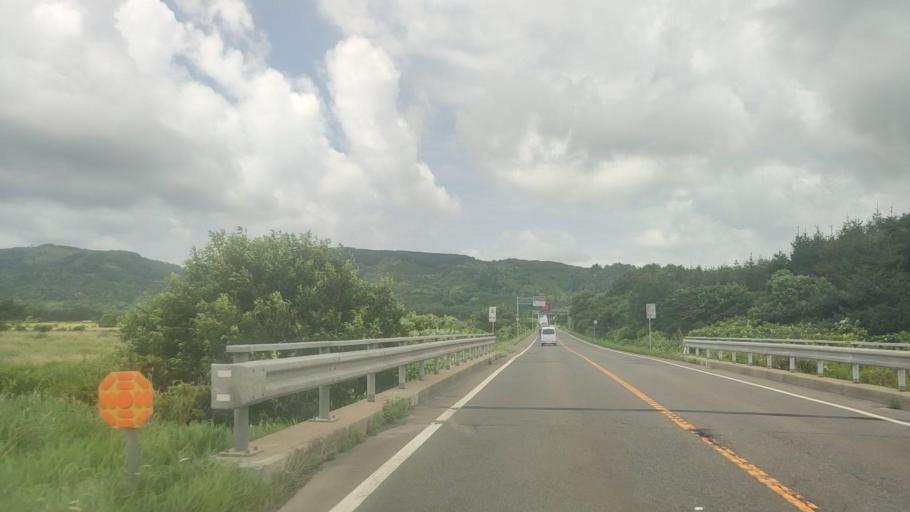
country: JP
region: Hokkaido
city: Niseko Town
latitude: 42.5822
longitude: 140.4532
